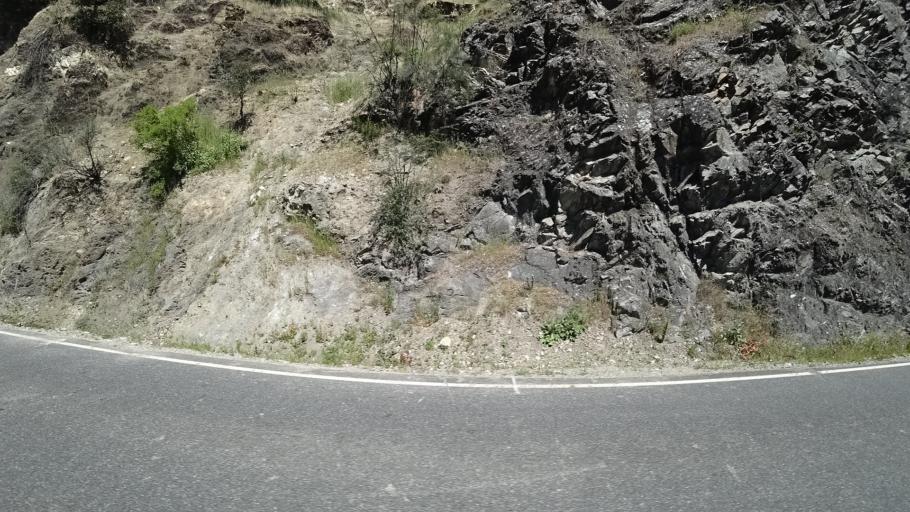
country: US
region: California
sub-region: Trinity County
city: Weaverville
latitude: 40.7502
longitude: -123.0630
